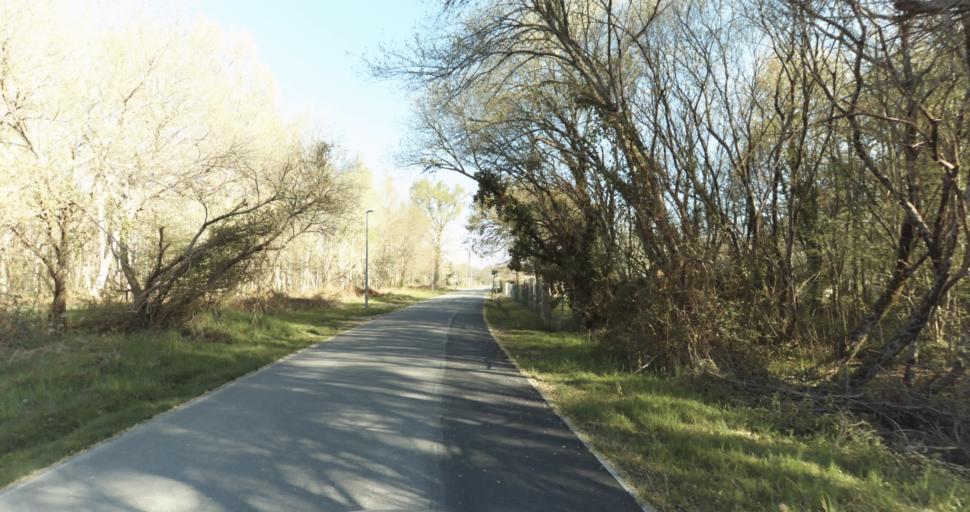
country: FR
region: Aquitaine
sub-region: Departement de la Gironde
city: Martignas-sur-Jalle
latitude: 44.8049
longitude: -0.8435
